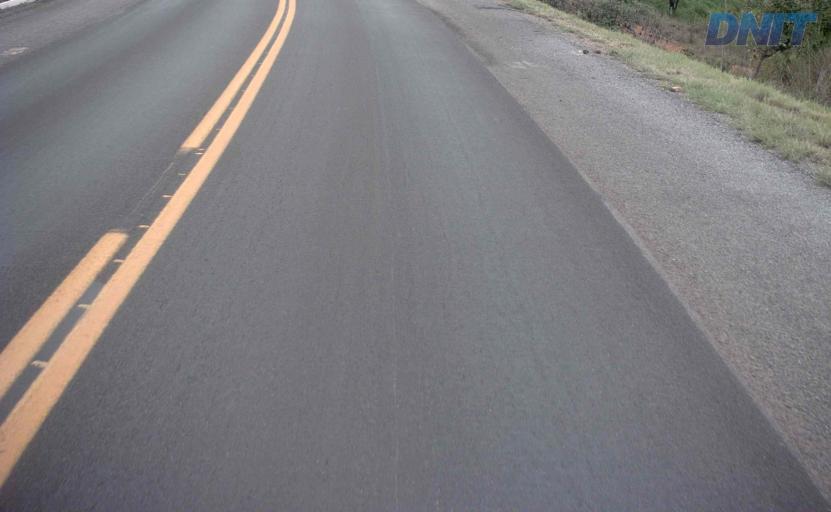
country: BR
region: Goias
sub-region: Barro Alto
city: Barro Alto
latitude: -15.2199
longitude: -48.6467
